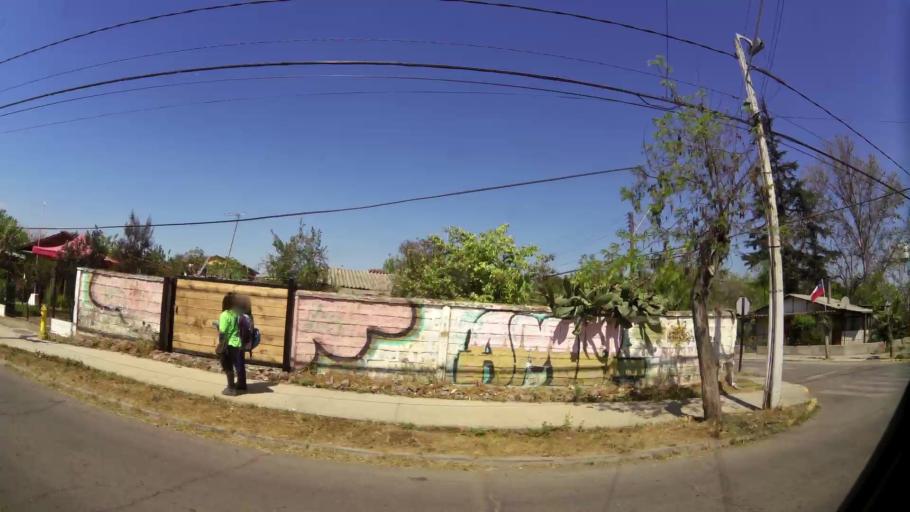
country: CL
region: Santiago Metropolitan
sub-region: Provincia de Talagante
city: Penaflor
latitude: -33.5693
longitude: -70.8099
